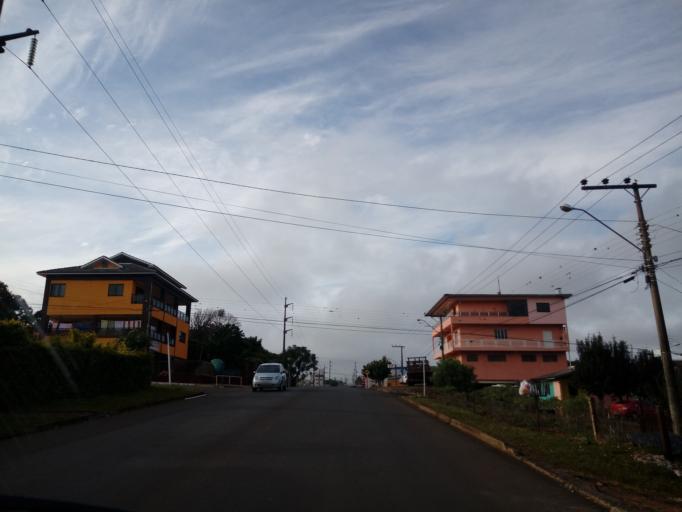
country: BR
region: Santa Catarina
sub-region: Chapeco
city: Chapeco
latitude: -27.0788
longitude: -52.6360
